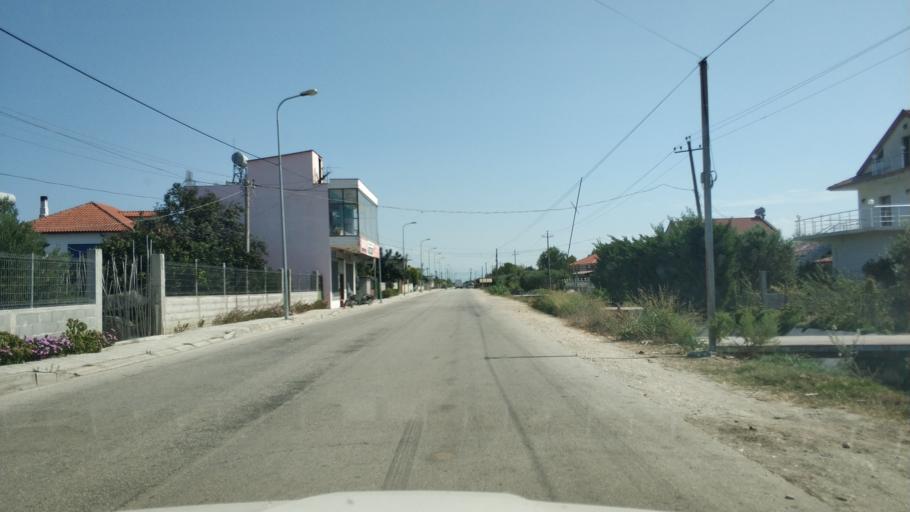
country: AL
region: Fier
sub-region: Rrethi i Lushnjes
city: Gradishte
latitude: 40.8842
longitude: 19.5772
